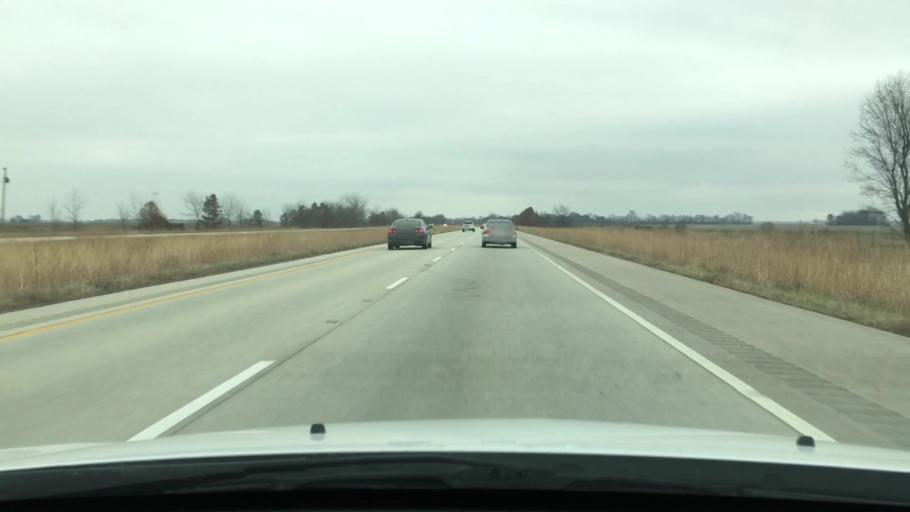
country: US
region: Illinois
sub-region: Sangamon County
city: New Berlin
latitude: 39.7410
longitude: -89.8413
